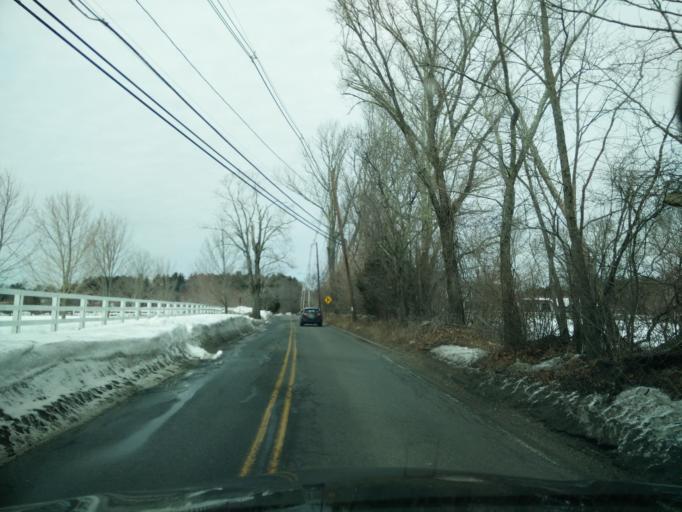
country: US
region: Massachusetts
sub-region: Norfolk County
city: Westwood
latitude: 42.1845
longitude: -71.2461
